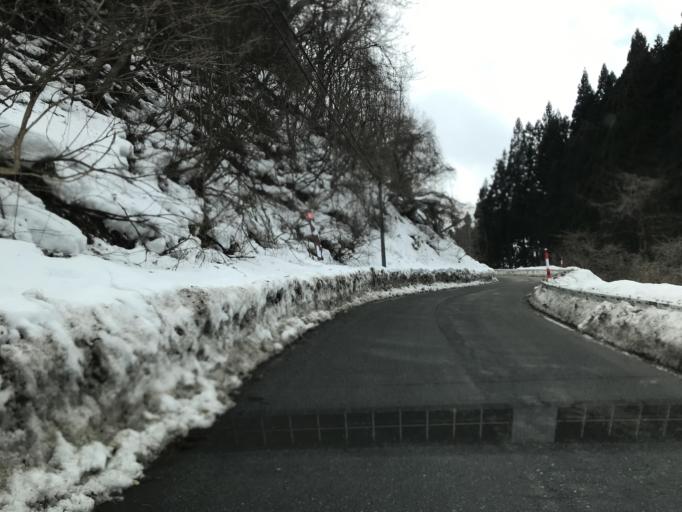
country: JP
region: Miyagi
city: Furukawa
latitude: 38.7275
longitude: 140.7621
